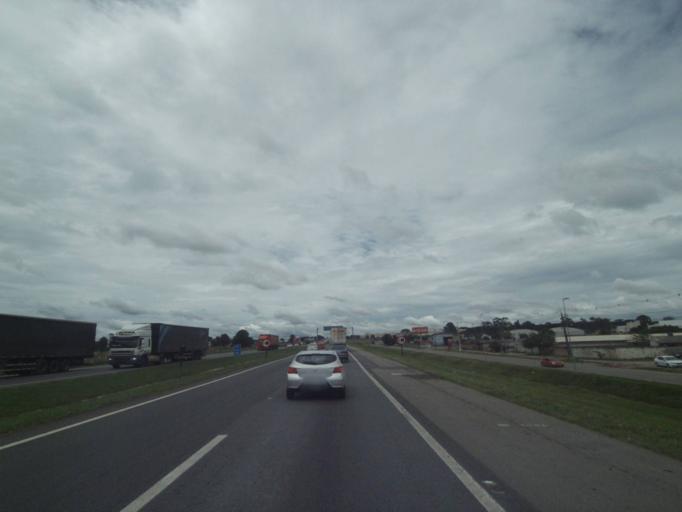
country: BR
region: Parana
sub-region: Piraquara
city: Piraquara
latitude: -25.5051
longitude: -49.1234
